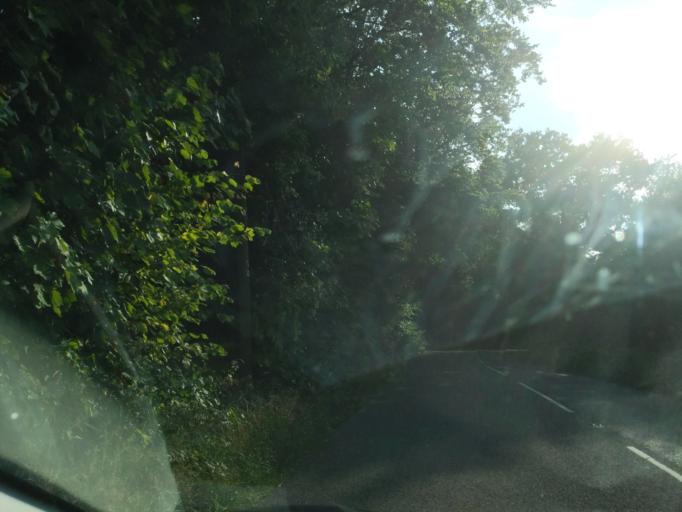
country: GB
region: England
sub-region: Devon
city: Great Torrington
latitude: 50.9764
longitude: -4.0548
